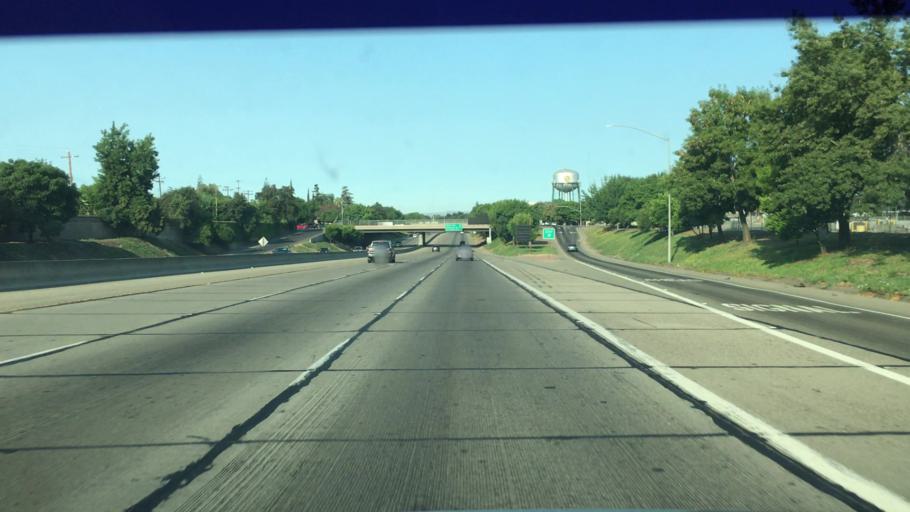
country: US
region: California
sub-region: San Joaquin County
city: Garden Acres
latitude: 37.9606
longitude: -121.2504
